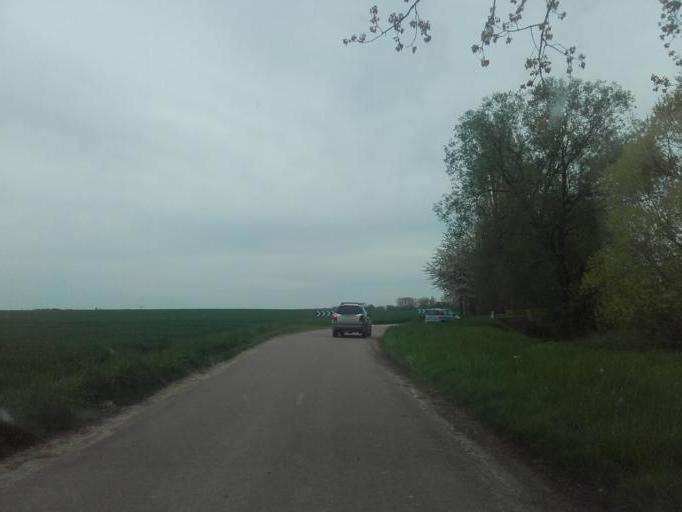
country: FR
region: Bourgogne
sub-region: Departement de la Cote-d'Or
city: Bligny-les-Beaune
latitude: 46.9760
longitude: 4.8632
